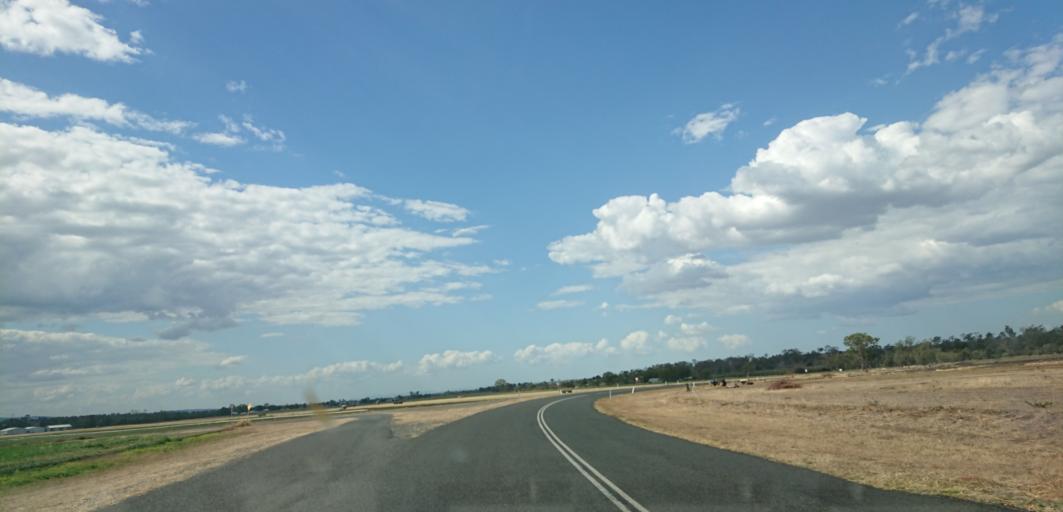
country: AU
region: Queensland
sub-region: Lockyer Valley
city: Gatton
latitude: -27.6259
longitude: 152.1931
